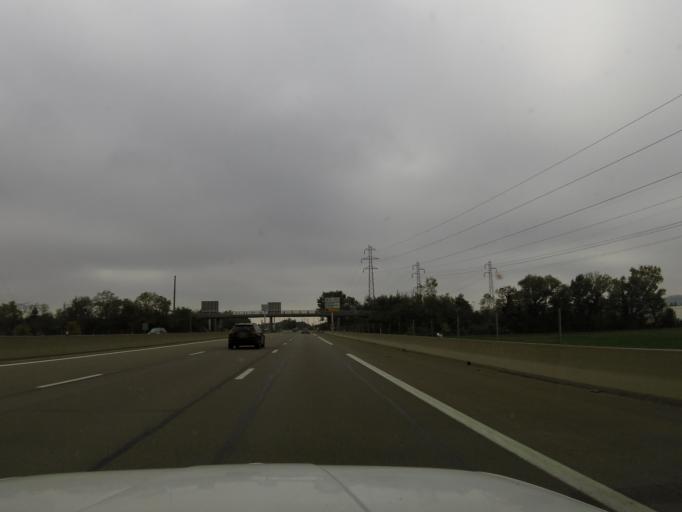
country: FR
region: Rhone-Alpes
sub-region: Departement de l'Ain
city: Beynost
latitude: 45.8237
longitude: 5.0024
